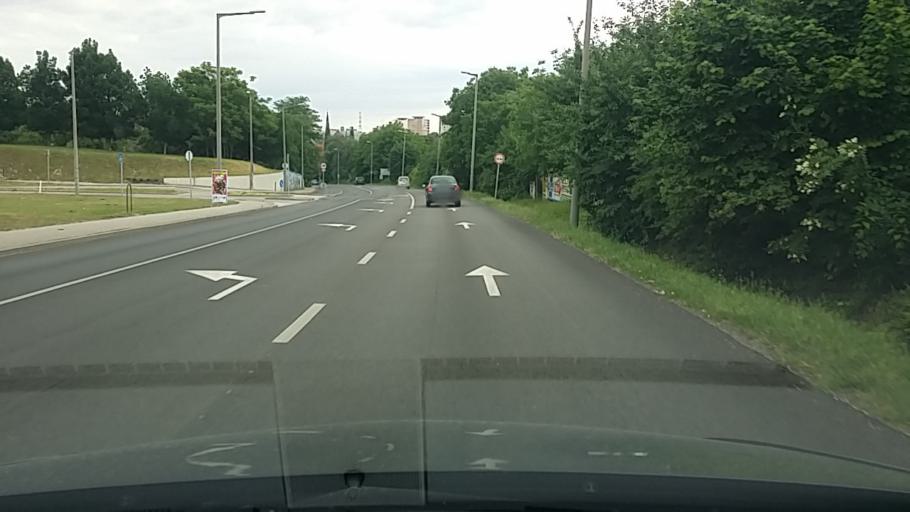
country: HU
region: Fejer
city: dunaujvaros
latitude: 46.9766
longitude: 18.9220
